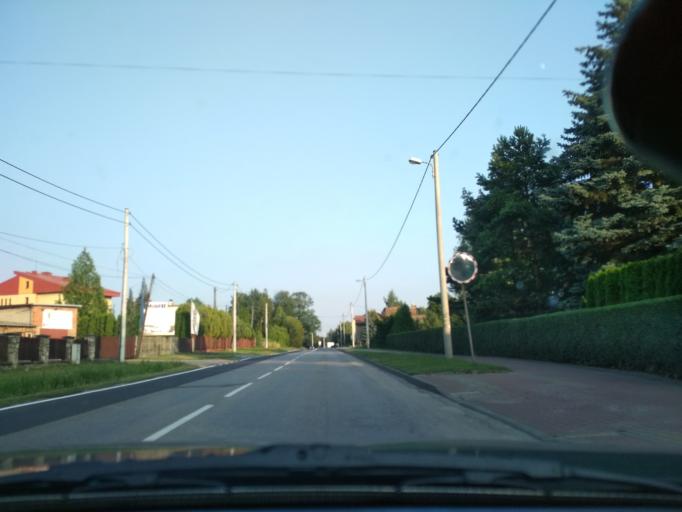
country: PL
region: Silesian Voivodeship
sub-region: Powiat zawiercianski
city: Ogrodzieniec
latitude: 50.4587
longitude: 19.4994
